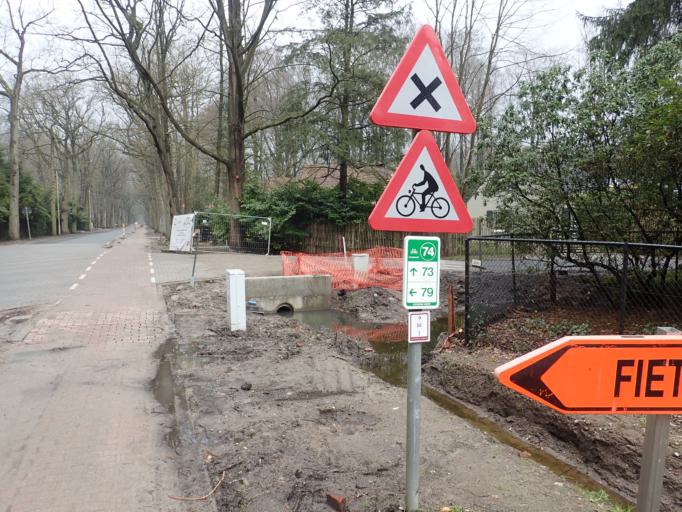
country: BE
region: Flanders
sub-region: Provincie Antwerpen
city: Kalmthout
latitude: 51.3494
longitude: 4.4568
